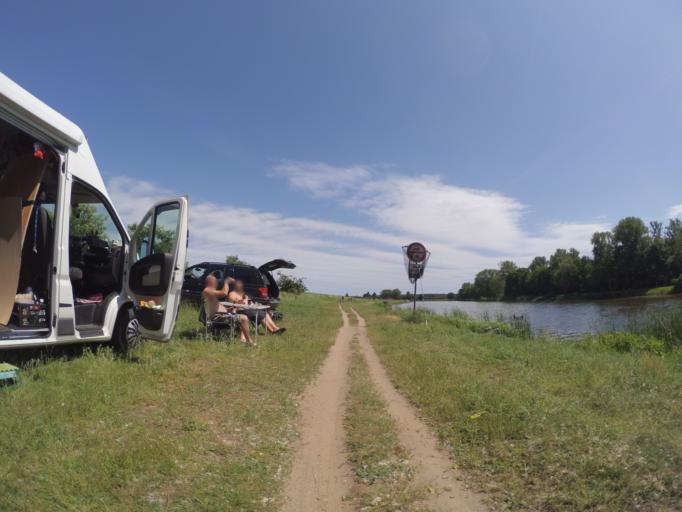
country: CZ
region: Central Bohemia
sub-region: Okres Nymburk
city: Sadska
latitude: 50.1678
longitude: 14.9532
